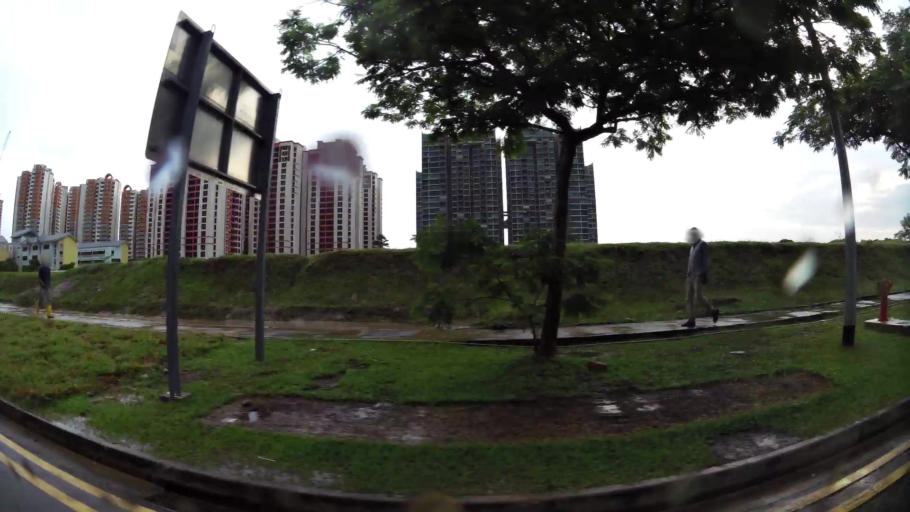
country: MY
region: Johor
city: Kampung Pasir Gudang Baru
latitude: 1.3909
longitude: 103.8725
